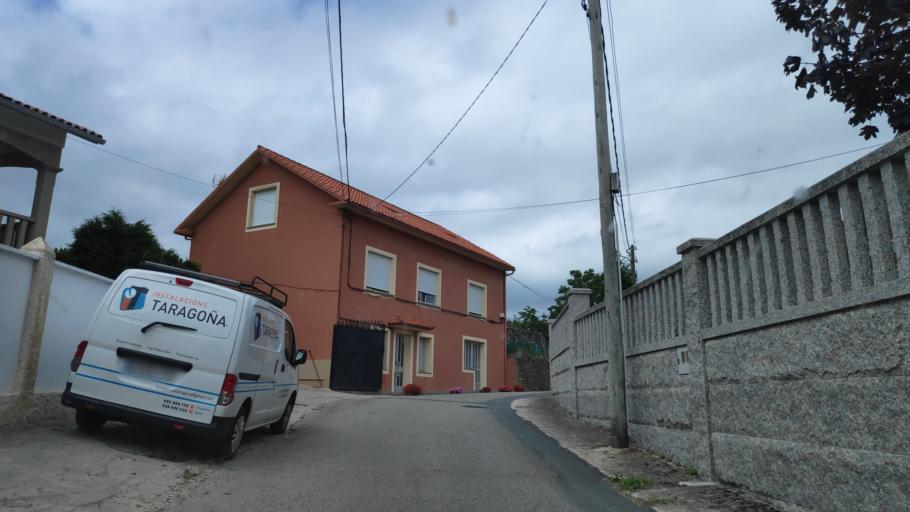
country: ES
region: Galicia
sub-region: Provincia da Coruna
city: Rianxo
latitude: 42.6725
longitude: -8.8135
